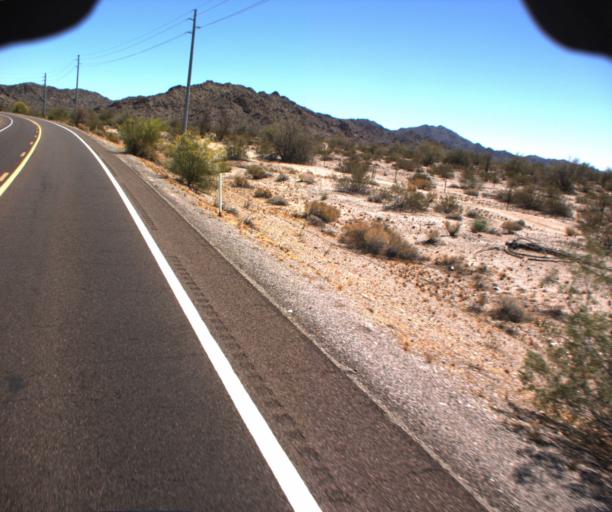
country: US
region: Arizona
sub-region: La Paz County
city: Salome
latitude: 33.7245
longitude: -113.6901
